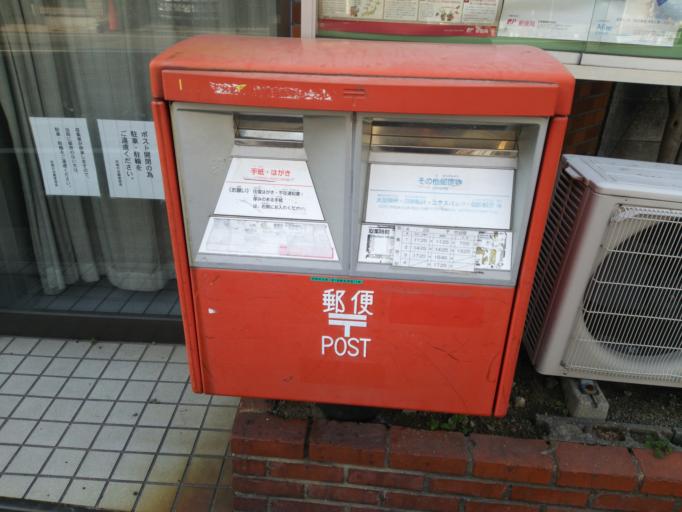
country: JP
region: Hyogo
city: Amagasaki
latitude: 34.7209
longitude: 135.4068
